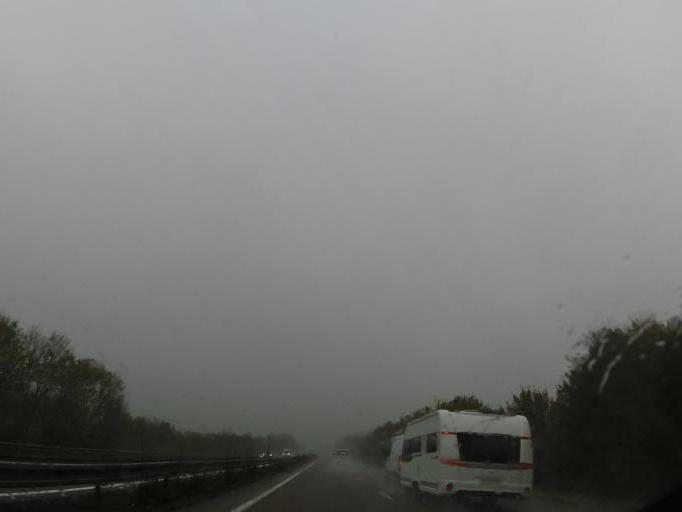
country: FR
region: Picardie
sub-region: Departement de l'Aisne
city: Brasles
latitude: 49.0896
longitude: 3.4219
